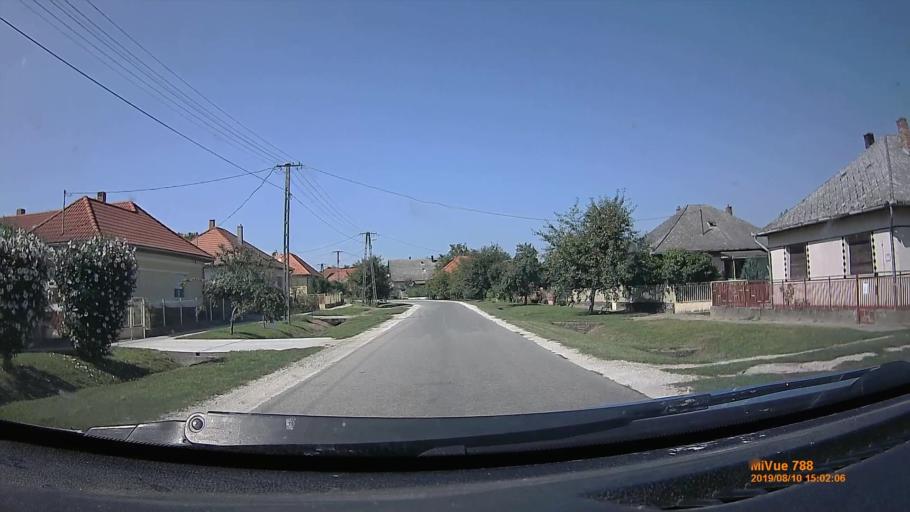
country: HU
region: Somogy
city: Lengyeltoti
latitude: 46.6537
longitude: 17.5766
